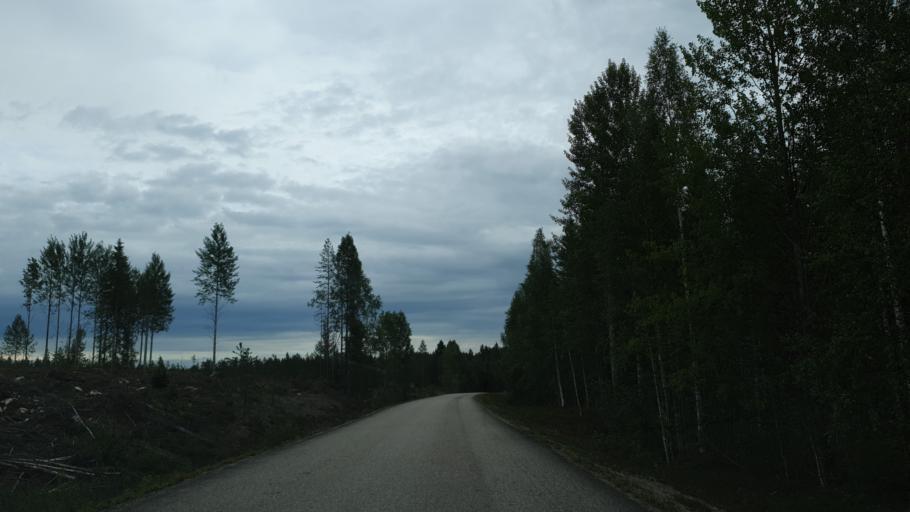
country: FI
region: Kainuu
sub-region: Kehys-Kainuu
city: Kuhmo
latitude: 64.3521
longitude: 29.1015
